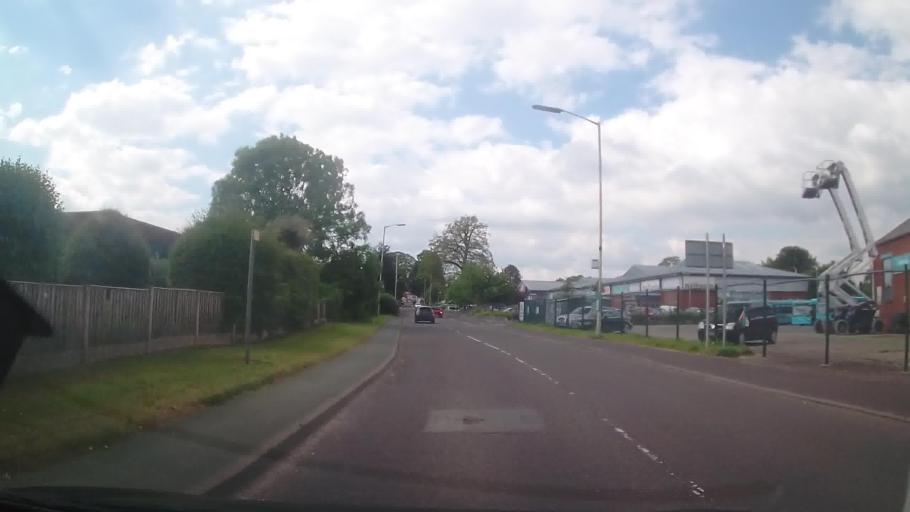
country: GB
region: England
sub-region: Shropshire
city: Oswestry
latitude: 52.8546
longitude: -3.0486
